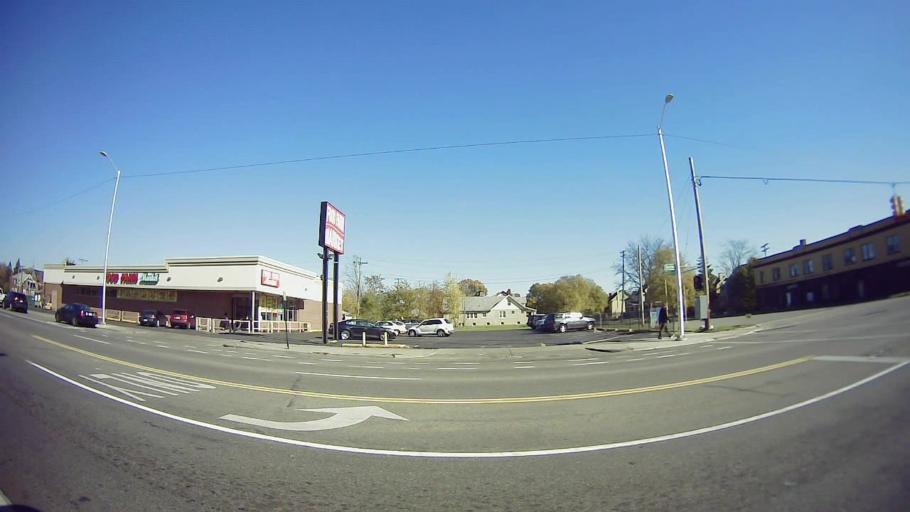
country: US
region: Michigan
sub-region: Wayne County
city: Highland Park
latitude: 42.3781
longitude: -83.1231
